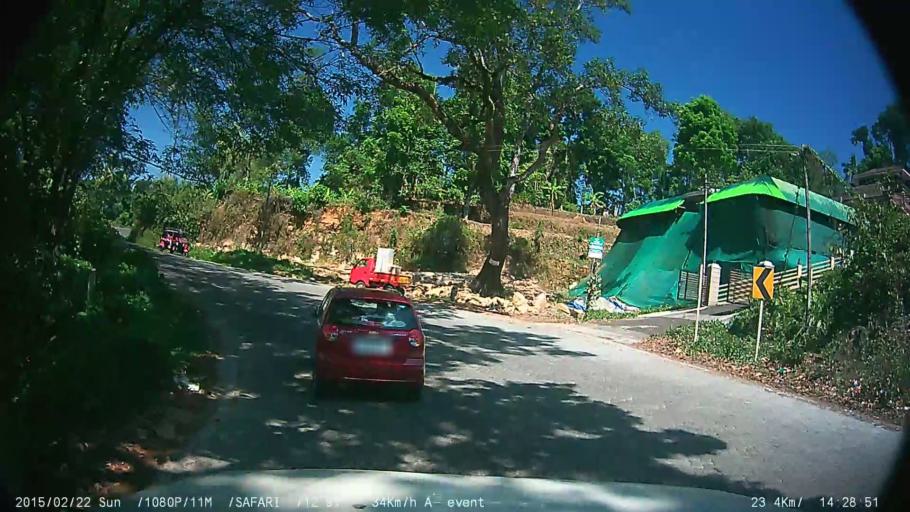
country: IN
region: Kerala
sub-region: Kottayam
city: Erattupetta
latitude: 9.5663
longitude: 76.7413
